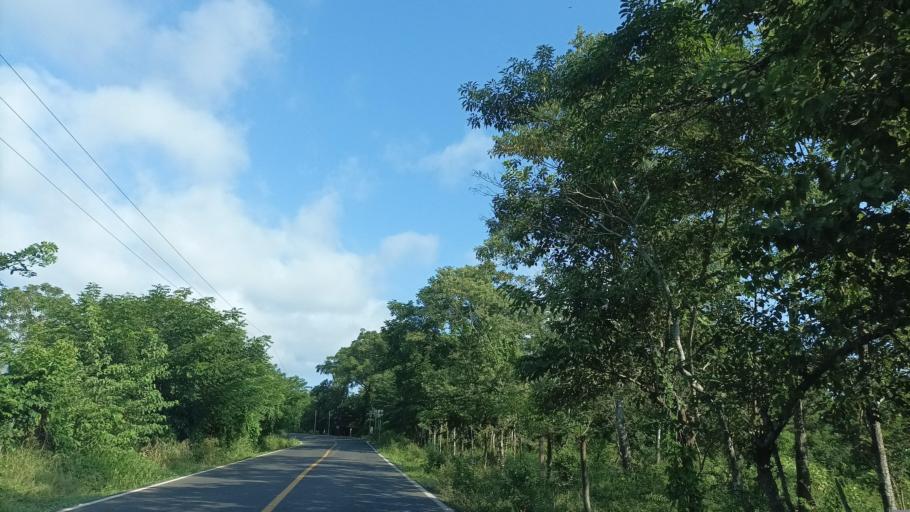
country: MX
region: Veracruz
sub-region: Chinameca
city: Chacalapa
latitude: 18.1638
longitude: -94.6578
